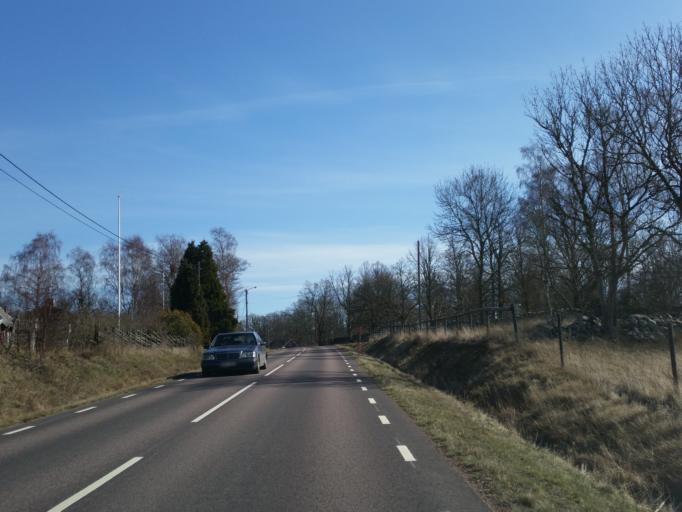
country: SE
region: Kalmar
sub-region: Monsteras Kommun
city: Timmernabben
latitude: 56.8665
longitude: 16.4204
